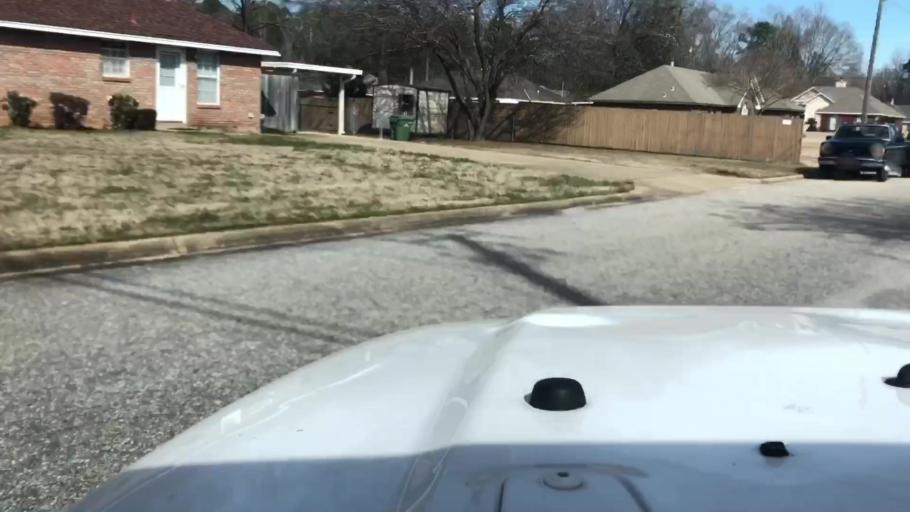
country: US
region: Alabama
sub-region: Elmore County
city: Blue Ridge
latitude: 32.4098
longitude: -86.1960
